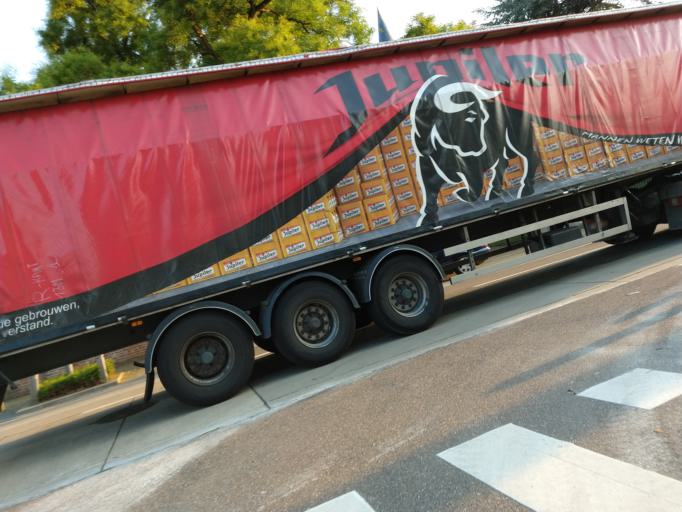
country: BE
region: Flanders
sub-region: Provincie Vlaams-Brabant
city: Hoegaarden
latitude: 50.7740
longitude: 4.8958
